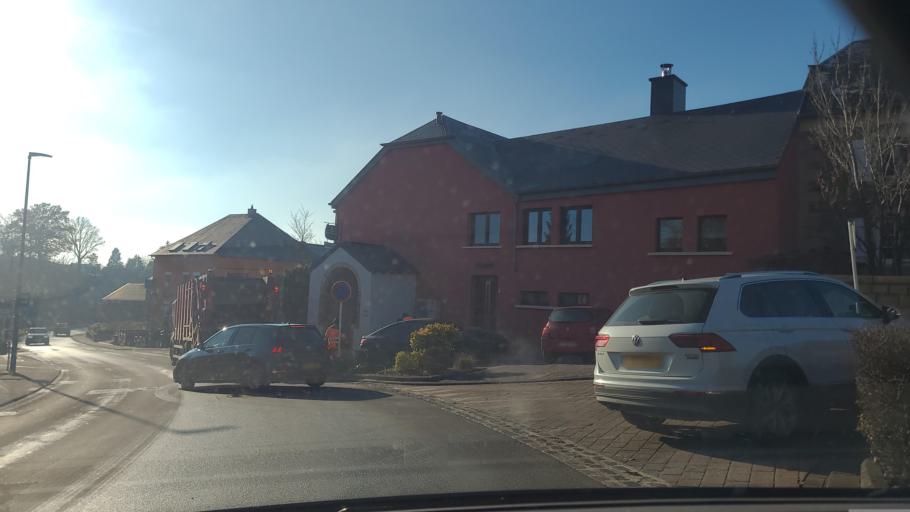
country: LU
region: Luxembourg
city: Hautcharage
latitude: 49.5753
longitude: 5.9093
